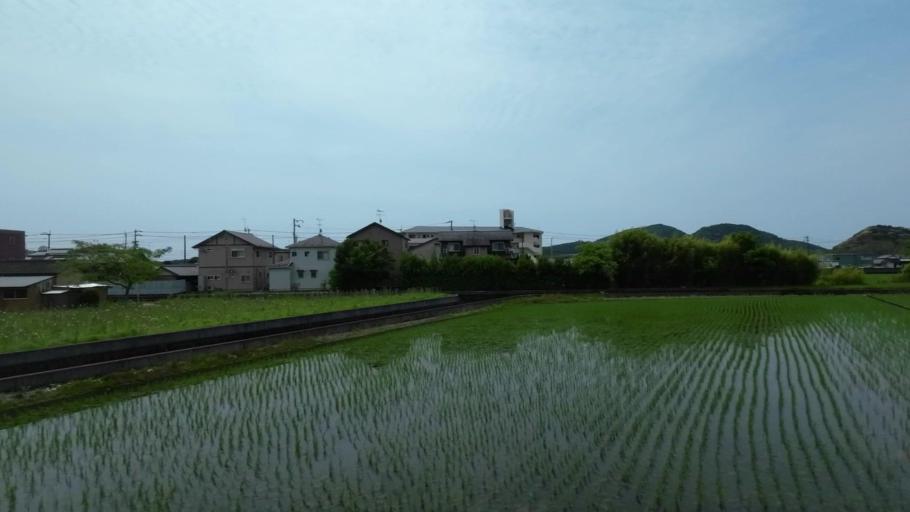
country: JP
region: Kochi
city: Kochi-shi
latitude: 33.5784
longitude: 133.6279
